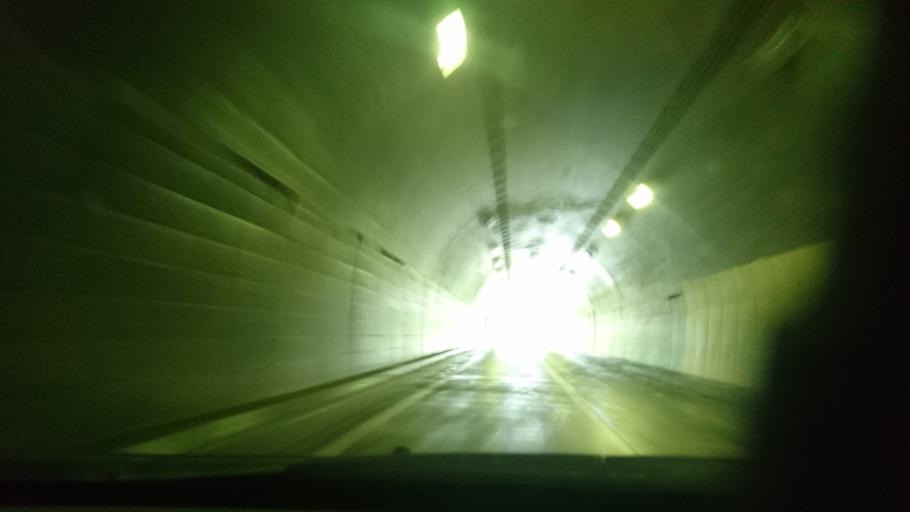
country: JP
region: Akita
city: Yuzawa
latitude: 39.1512
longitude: 140.7607
